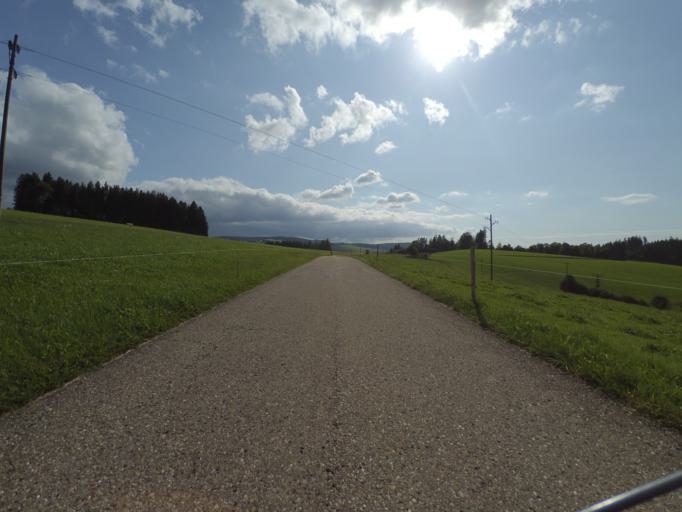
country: DE
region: Baden-Wuerttemberg
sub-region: Freiburg Region
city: Sankt Margen
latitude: 47.9777
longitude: 8.1024
